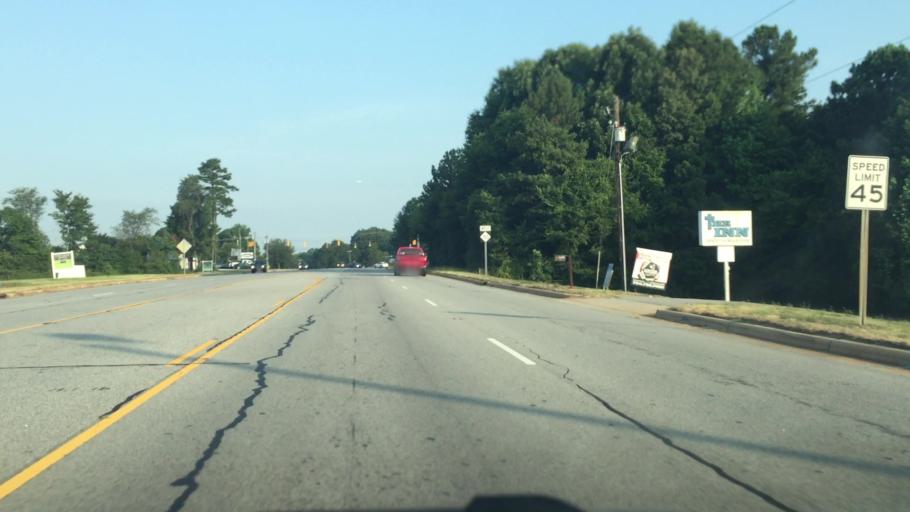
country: US
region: North Carolina
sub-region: Rowan County
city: Salisbury
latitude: 35.6625
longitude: -80.5018
